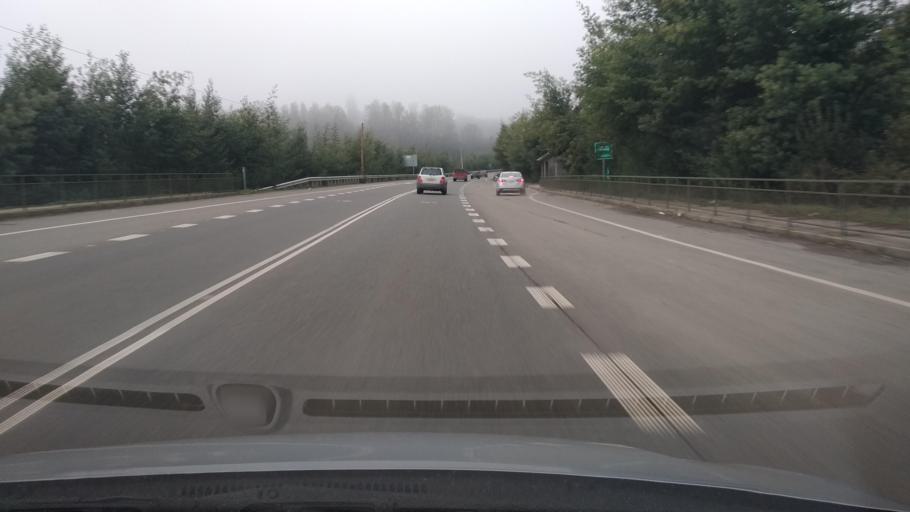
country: CL
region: Los Lagos
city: Las Animas
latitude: -39.7303
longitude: -73.1977
